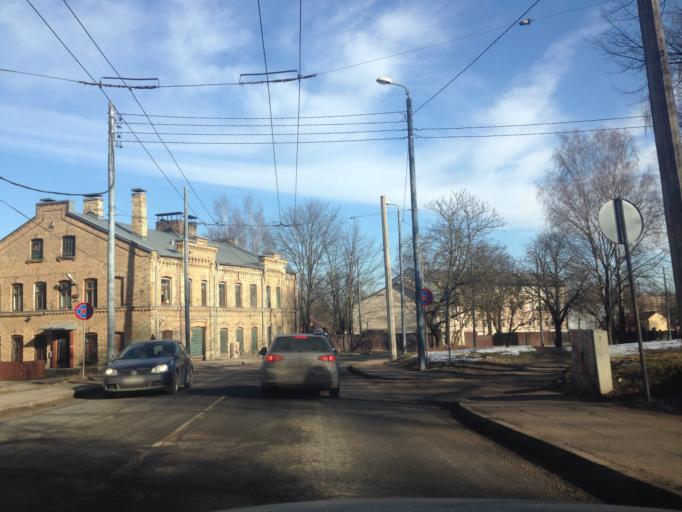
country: LV
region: Riga
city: Riga
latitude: 56.9288
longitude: 24.0949
